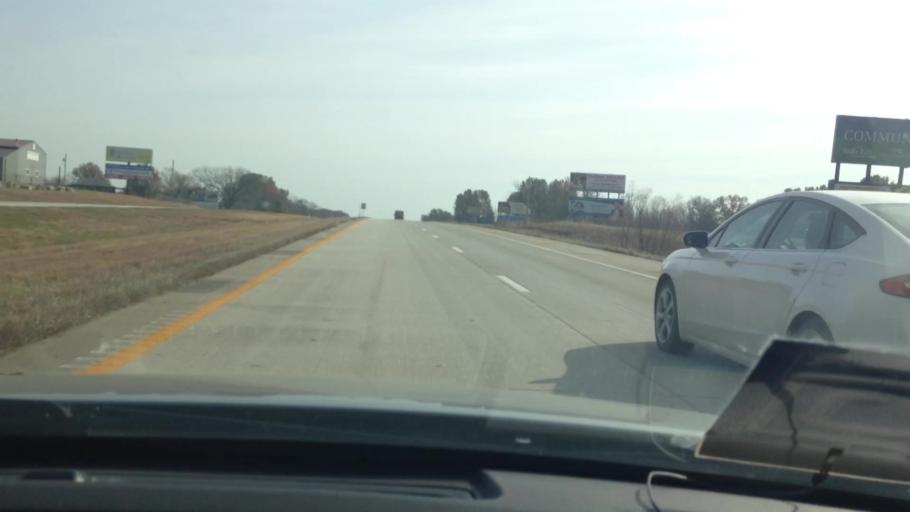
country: US
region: Missouri
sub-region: Henry County
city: Clinton
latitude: 38.4237
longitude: -93.8760
